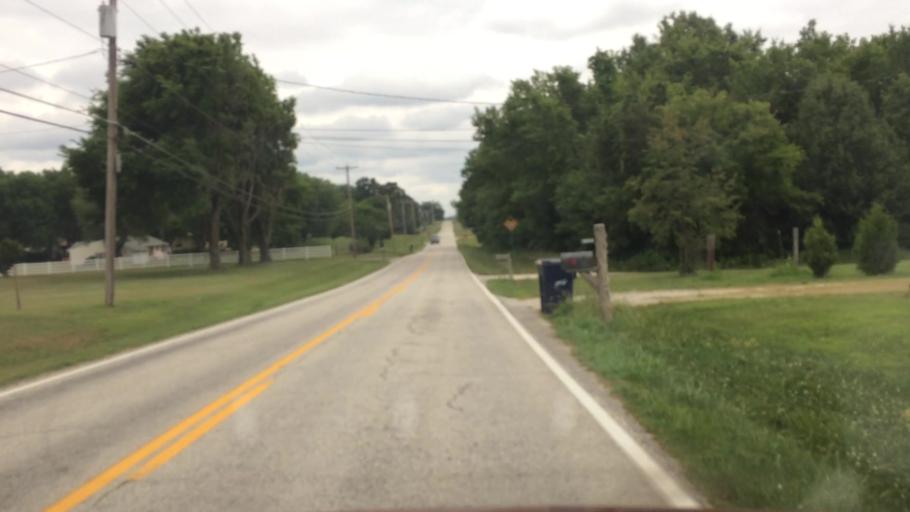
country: US
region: Missouri
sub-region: Greene County
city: Springfield
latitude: 37.2951
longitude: -93.2572
